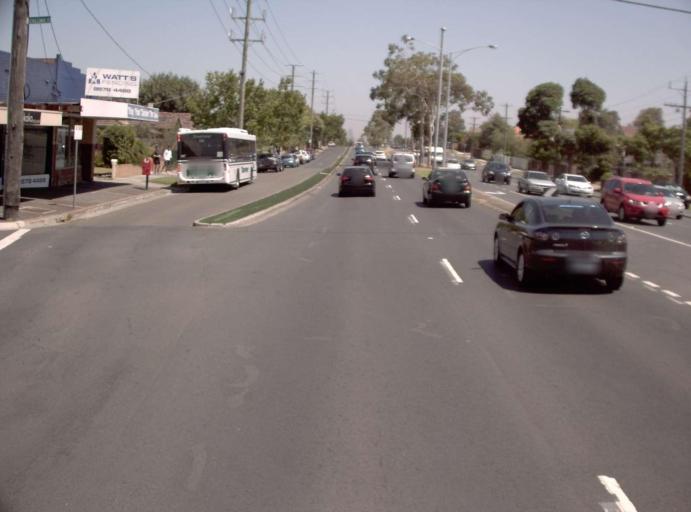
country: AU
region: Victoria
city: McKinnon
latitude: -37.9055
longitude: 145.0522
